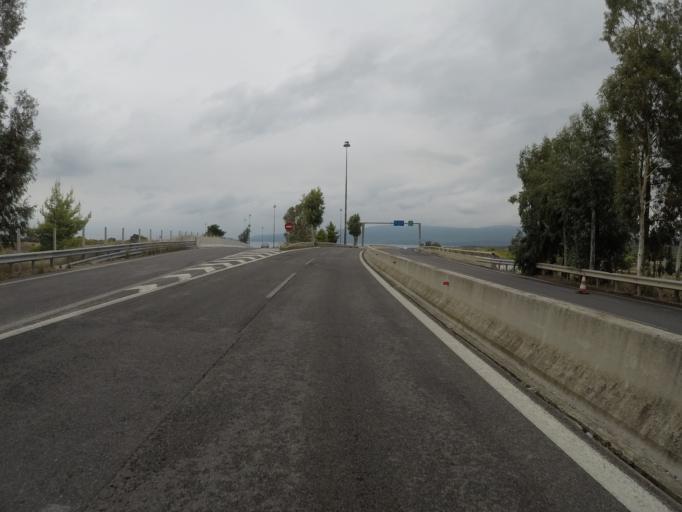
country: GR
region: Peloponnese
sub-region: Nomos Korinthias
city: Isthmia
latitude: 37.9262
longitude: 22.9986
